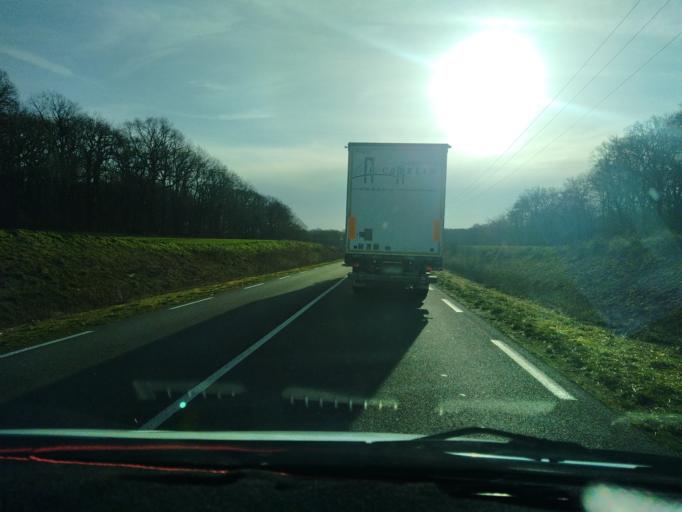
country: FR
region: Franche-Comte
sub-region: Departement de la Haute-Saone
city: Gray
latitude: 47.4235
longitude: 5.6150
